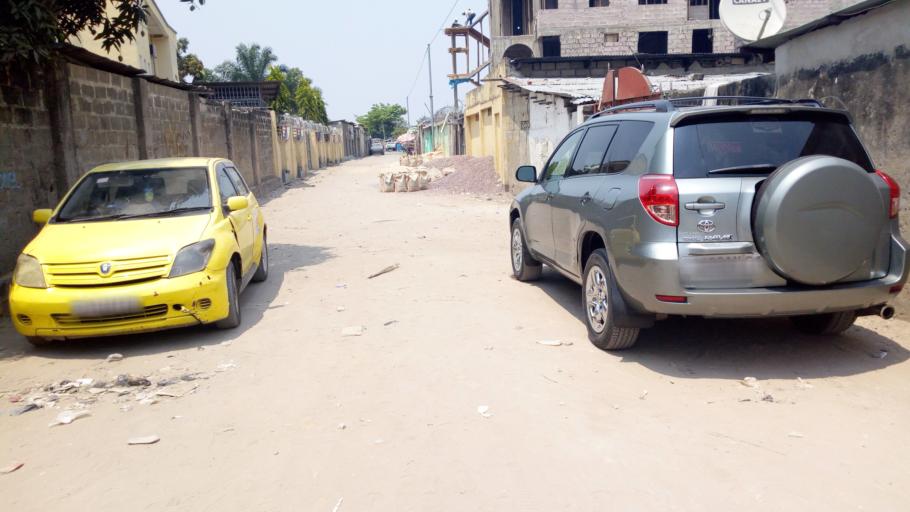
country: CD
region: Kinshasa
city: Kinshasa
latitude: -4.3162
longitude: 15.2943
